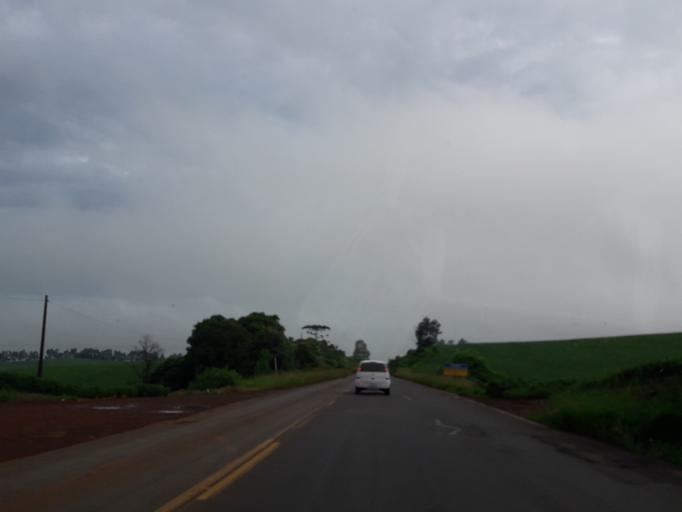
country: AR
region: Misiones
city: Bernardo de Irigoyen
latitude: -26.3188
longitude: -53.5499
